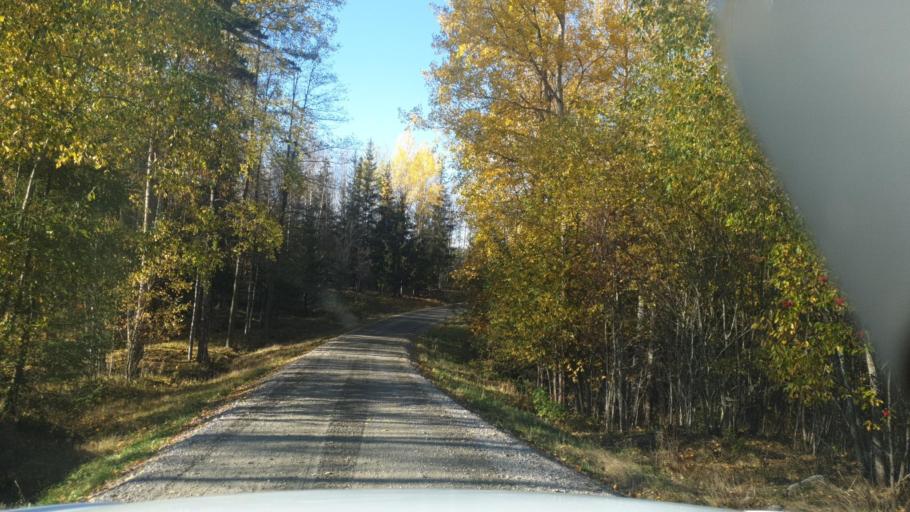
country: SE
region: Vaermland
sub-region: Arvika Kommun
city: Arvika
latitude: 59.5930
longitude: 12.8076
